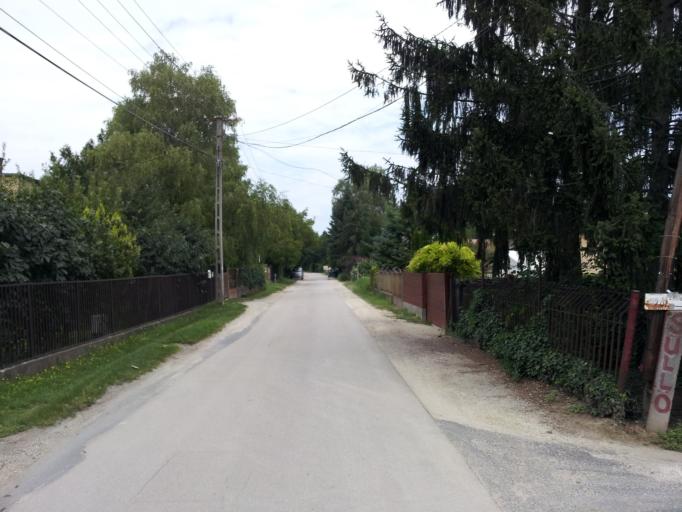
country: HU
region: Pest
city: Rackeve
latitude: 47.1687
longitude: 18.9513
